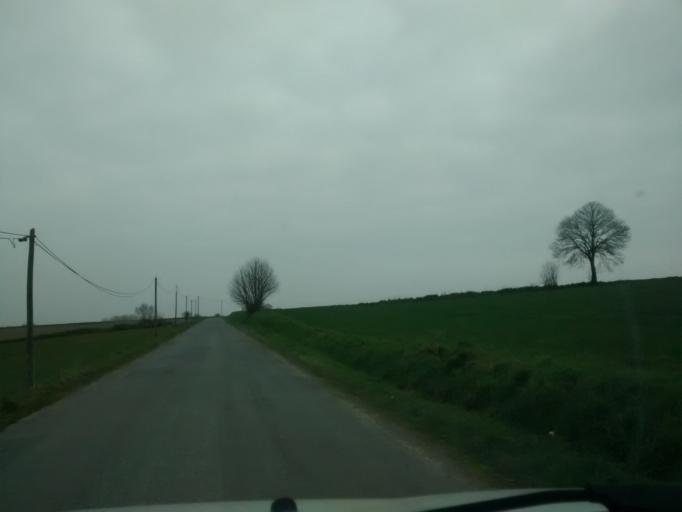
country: FR
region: Brittany
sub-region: Departement d'Ille-et-Vilaine
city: Bazouges-la-Perouse
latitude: 48.4026
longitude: -1.5708
